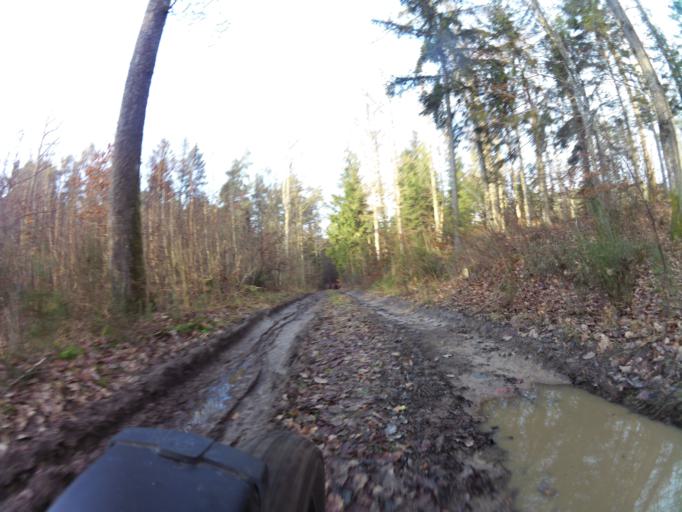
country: PL
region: West Pomeranian Voivodeship
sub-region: Powiat koszalinski
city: Polanow
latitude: 54.0838
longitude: 16.6469
